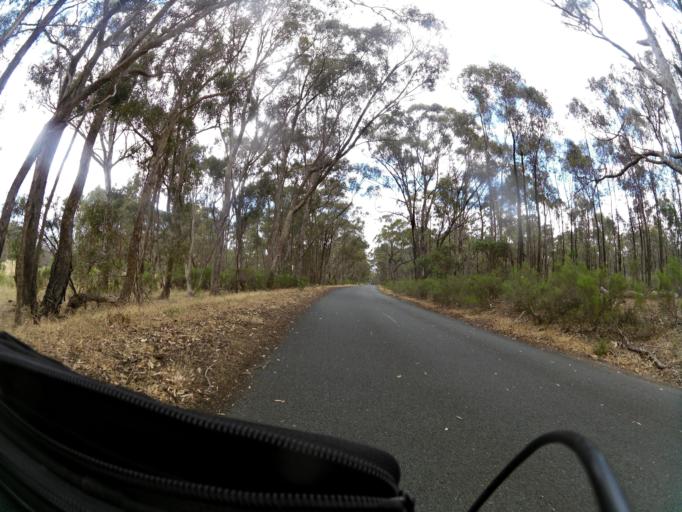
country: AU
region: Victoria
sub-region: Greater Shepparton
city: Shepparton
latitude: -36.6879
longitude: 145.1800
